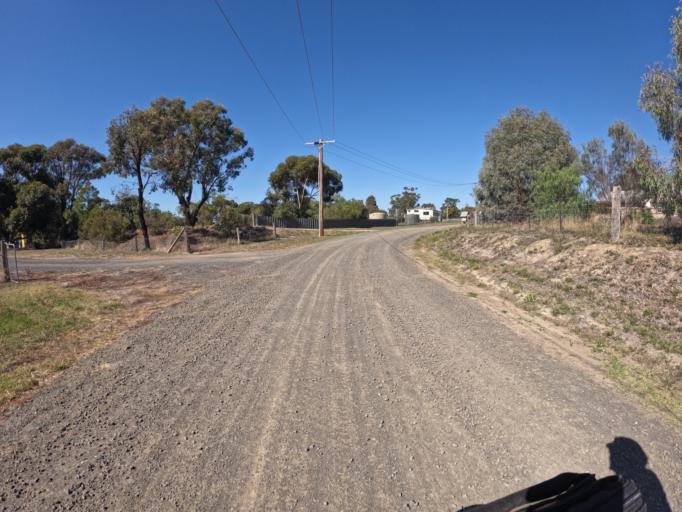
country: AU
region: Victoria
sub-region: Greater Bendigo
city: Kennington
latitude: -36.8262
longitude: 144.5848
